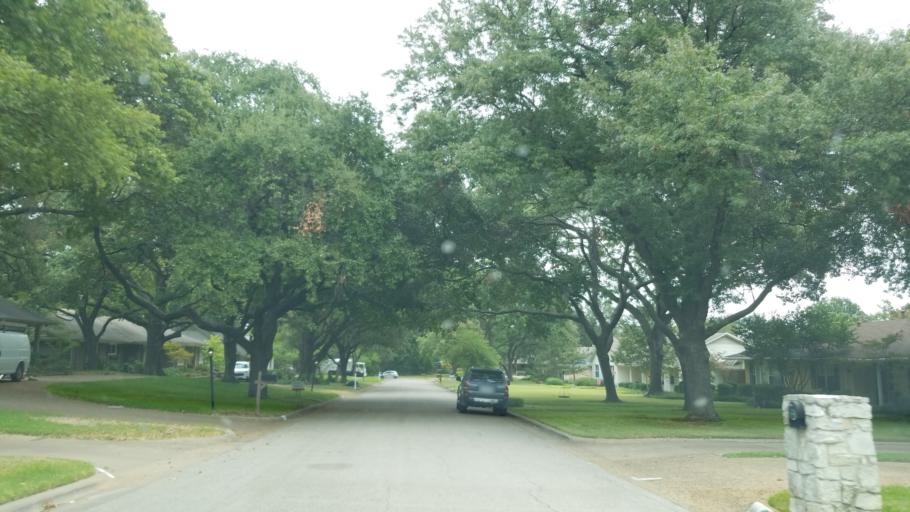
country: US
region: Texas
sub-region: Dallas County
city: Richardson
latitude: 32.9411
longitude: -96.7746
